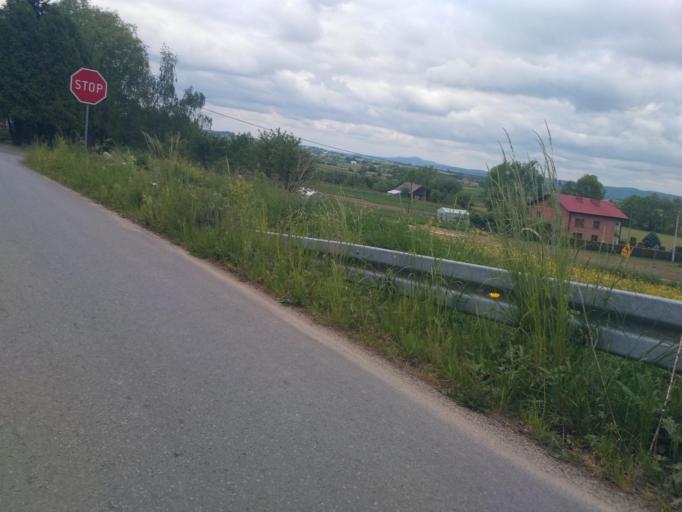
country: PL
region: Subcarpathian Voivodeship
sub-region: Powiat jasielski
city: Tarnowiec
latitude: 49.7152
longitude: 21.5824
